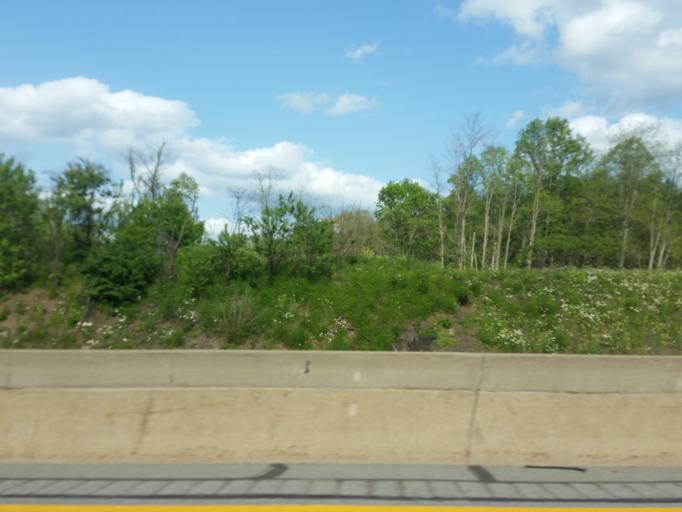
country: US
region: West Virginia
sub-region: Raleigh County
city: MacArthur
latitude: 37.7401
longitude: -81.2086
